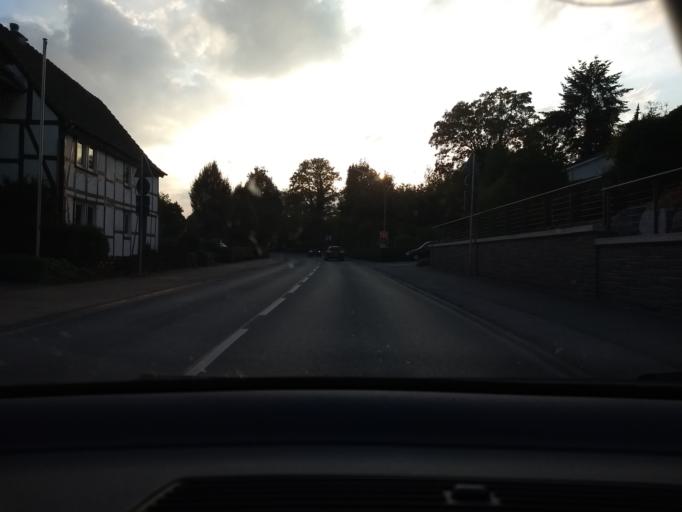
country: DE
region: North Rhine-Westphalia
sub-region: Regierungsbezirk Arnsberg
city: Arnsberg
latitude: 51.3559
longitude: 8.1668
